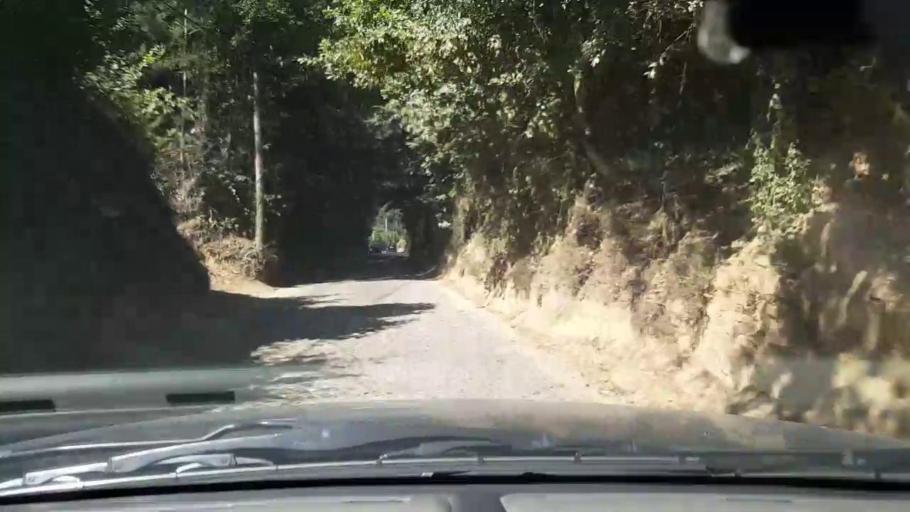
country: PT
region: Porto
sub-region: Matosinhos
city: Lavra
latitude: 41.2732
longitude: -8.6951
